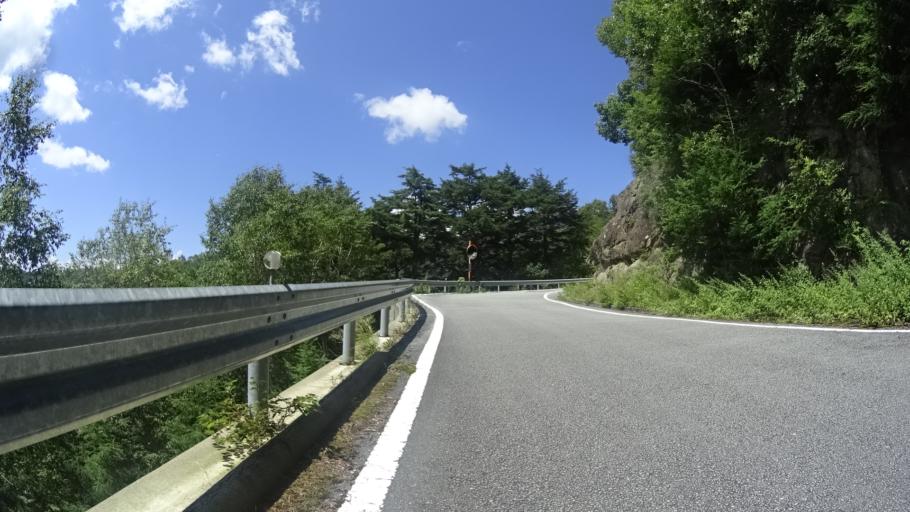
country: JP
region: Yamanashi
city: Enzan
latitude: 35.8483
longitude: 138.6426
